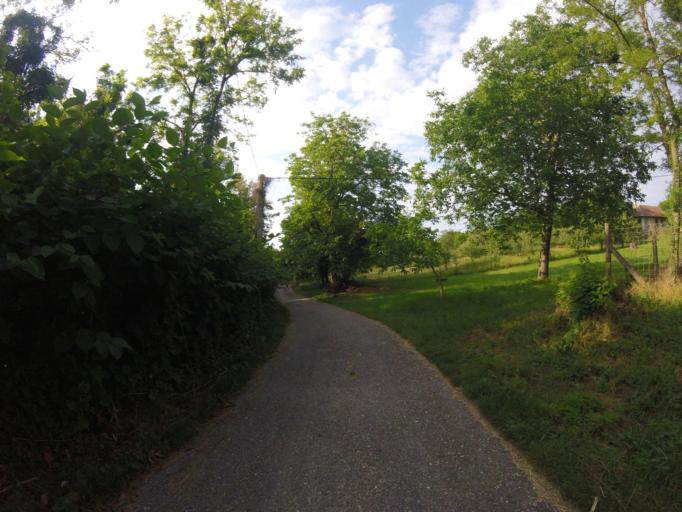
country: HU
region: Zala
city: Zalaszentgrot
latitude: 46.8854
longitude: 17.1268
